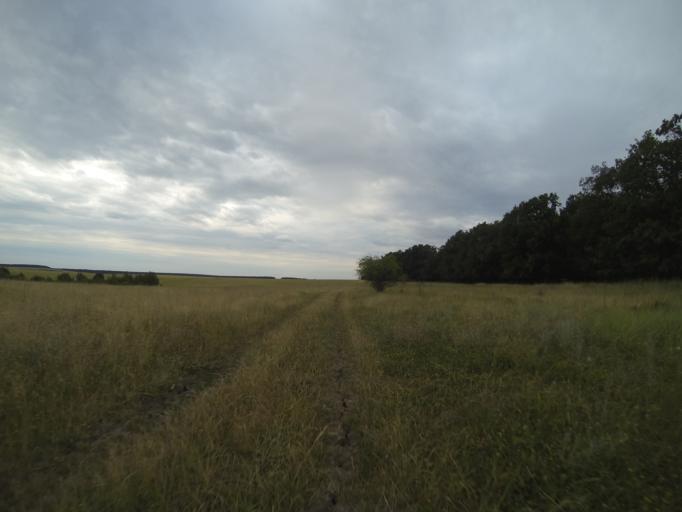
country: RO
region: Dolj
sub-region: Comuna Bradesti
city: Bradesti
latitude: 44.5464
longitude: 23.6497
